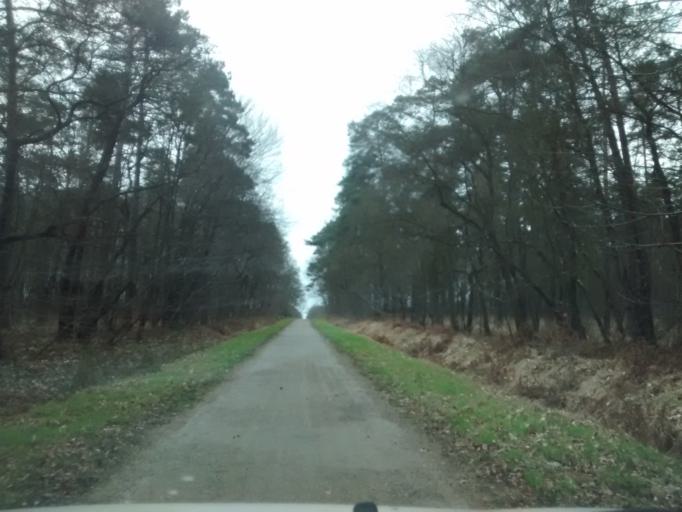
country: FR
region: Brittany
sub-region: Departement d'Ille-et-Vilaine
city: Fouillard
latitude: 48.1737
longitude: -1.5464
